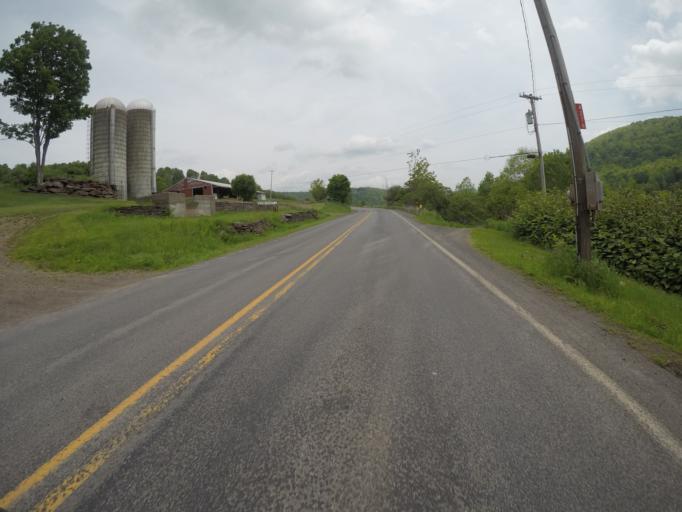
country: US
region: New York
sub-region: Delaware County
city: Delhi
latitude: 42.2704
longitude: -74.7440
